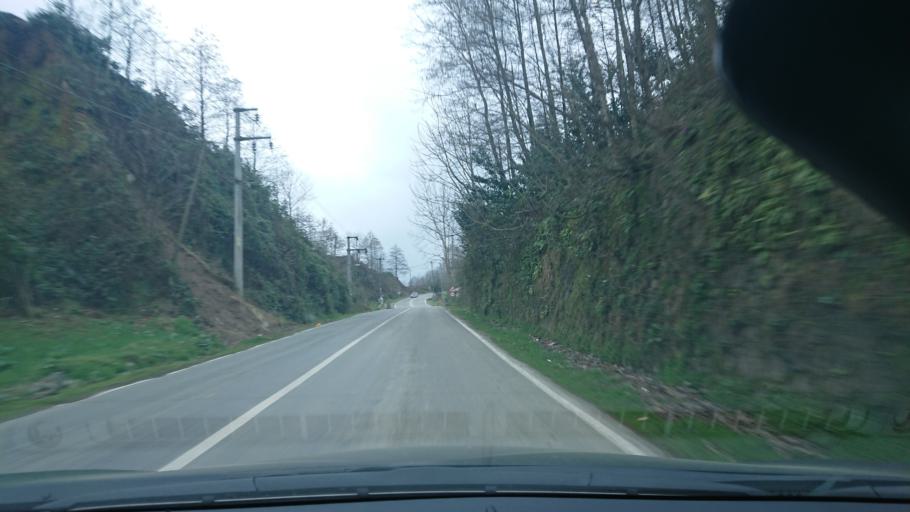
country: TR
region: Rize
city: Rize
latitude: 41.0128
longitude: 40.4924
